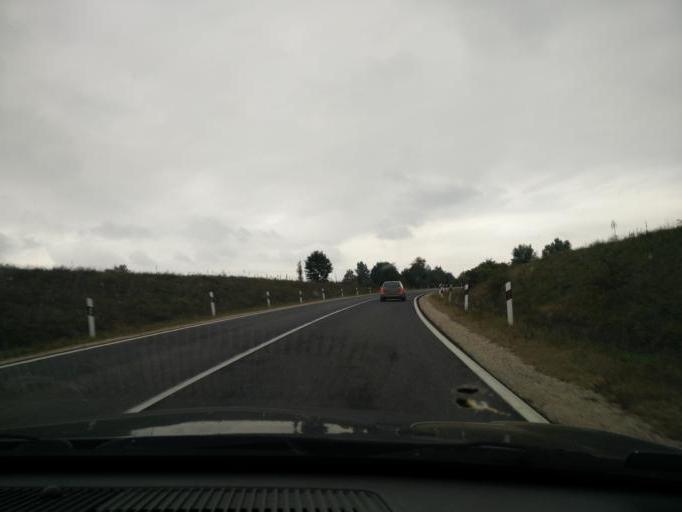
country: HU
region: Komarom-Esztergom
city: Kesztolc
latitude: 47.7195
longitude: 18.7738
